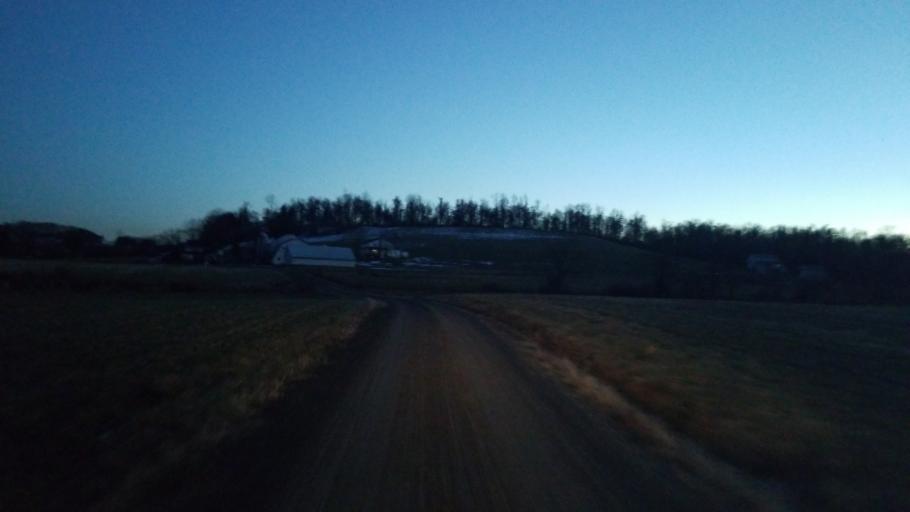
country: US
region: Pennsylvania
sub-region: Indiana County
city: Chevy Chase Heights
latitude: 40.8681
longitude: -79.2417
